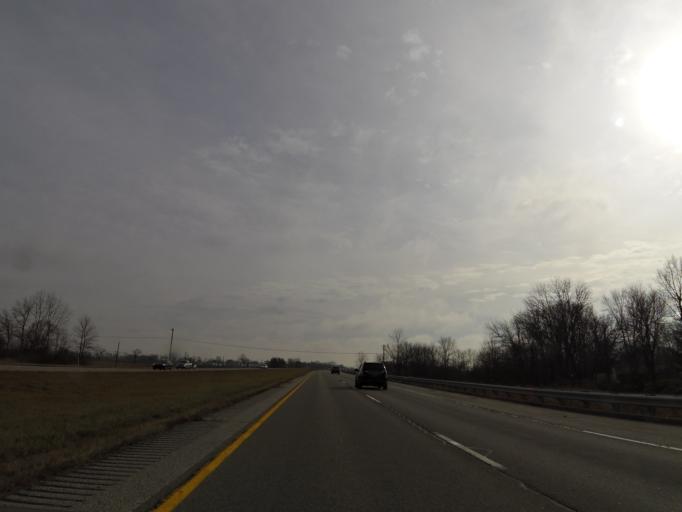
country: US
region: Indiana
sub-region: Hancock County
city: New Palestine
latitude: 39.6325
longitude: -85.8933
